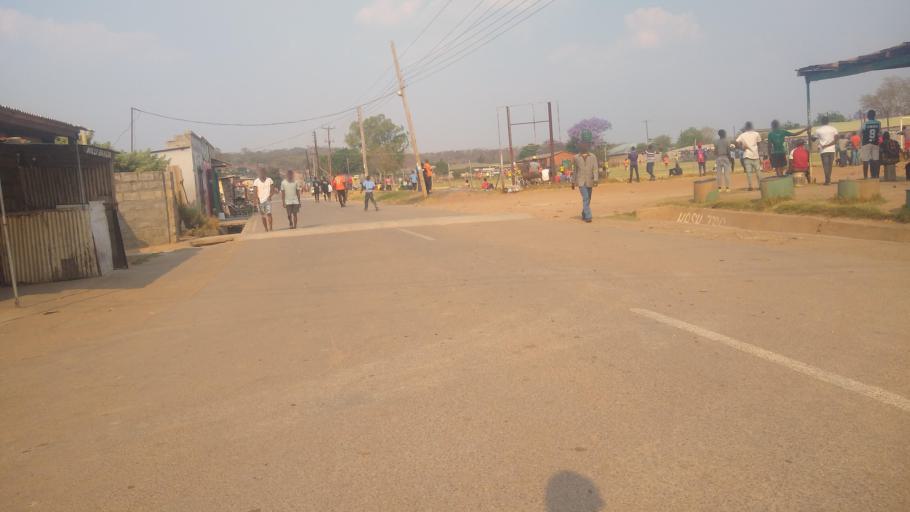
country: ZM
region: Lusaka
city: Lusaka
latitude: -15.4467
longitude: 28.3833
